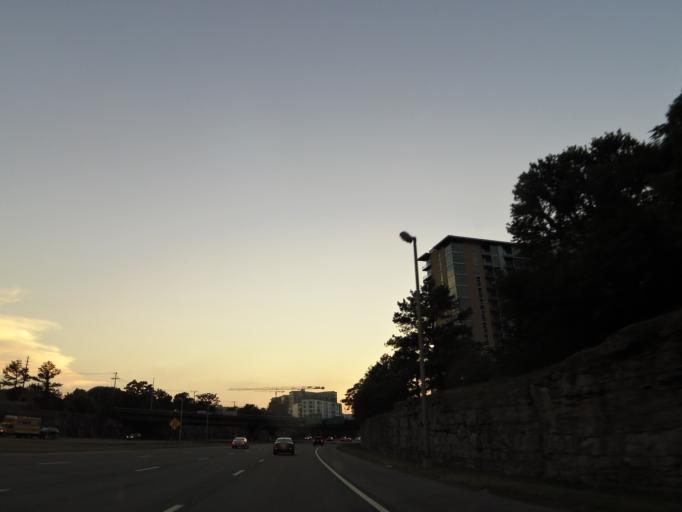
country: US
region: Tennessee
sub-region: Davidson County
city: Nashville
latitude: 36.1496
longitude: -86.7828
